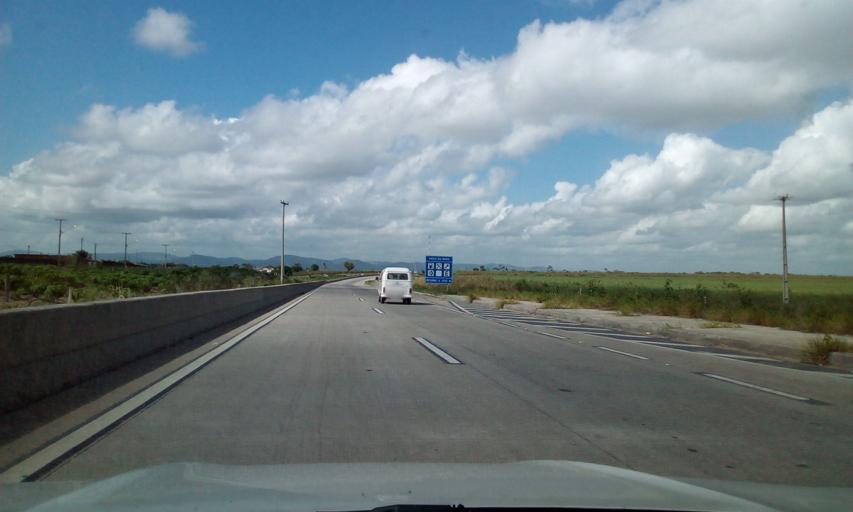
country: BR
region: Alagoas
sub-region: Messias
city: Messias
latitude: -9.3967
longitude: -35.8364
